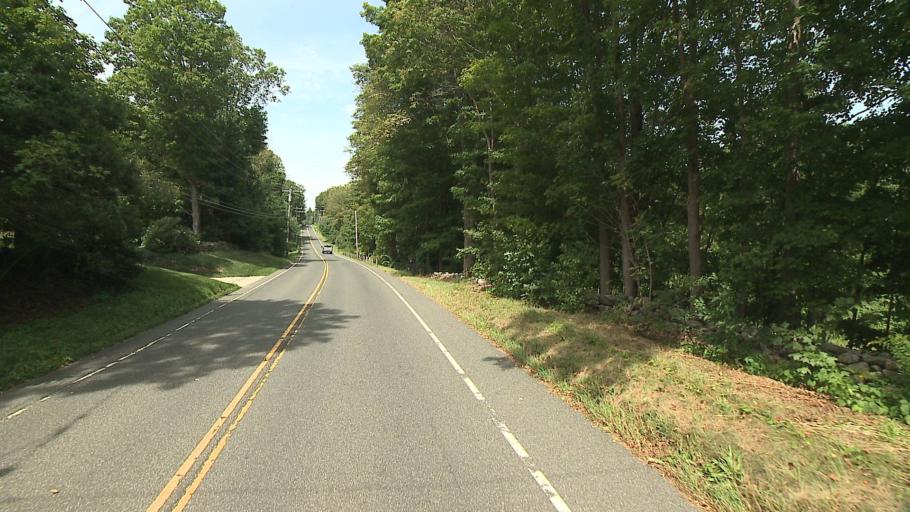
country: US
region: Connecticut
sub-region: Litchfield County
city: Woodbury
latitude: 41.5883
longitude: -73.2313
